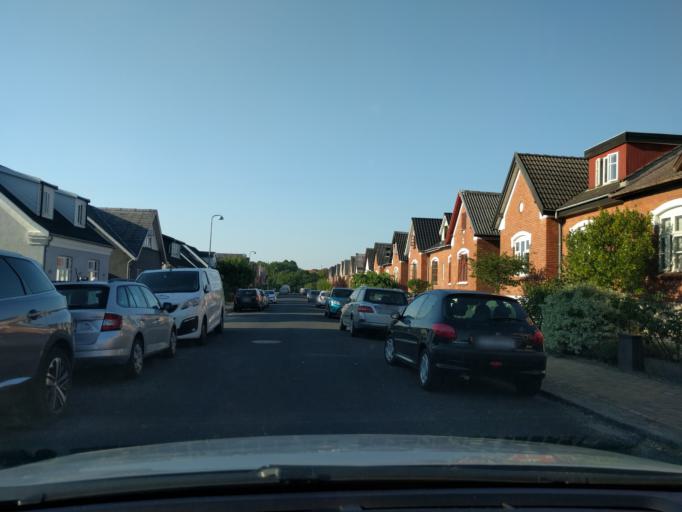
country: DK
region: South Denmark
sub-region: Odense Kommune
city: Odense
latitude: 55.4094
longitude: 10.3955
